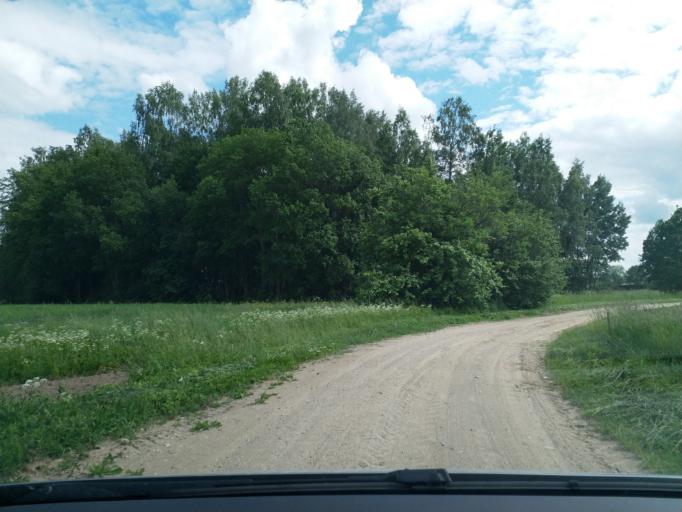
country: LV
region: Kuldigas Rajons
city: Kuldiga
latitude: 56.8471
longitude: 21.9480
